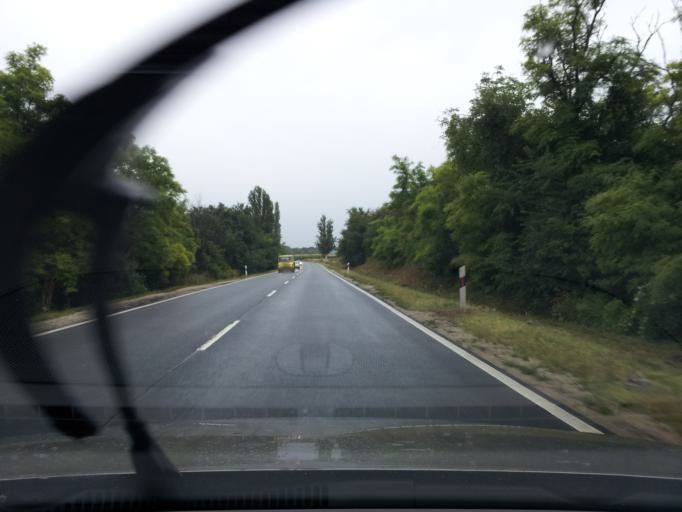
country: HU
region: Fejer
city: Lepseny
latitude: 47.0000
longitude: 18.1790
